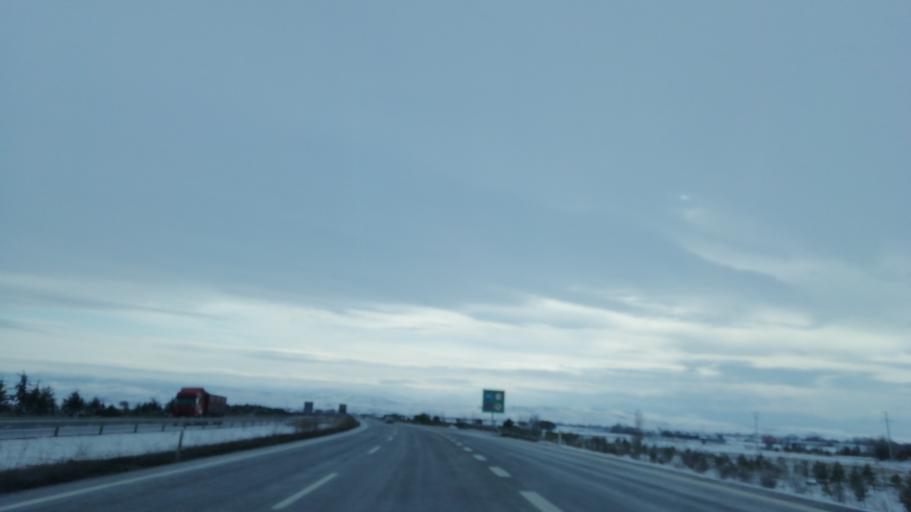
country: TR
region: Bolu
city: Gerede
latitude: 40.7737
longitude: 32.2055
